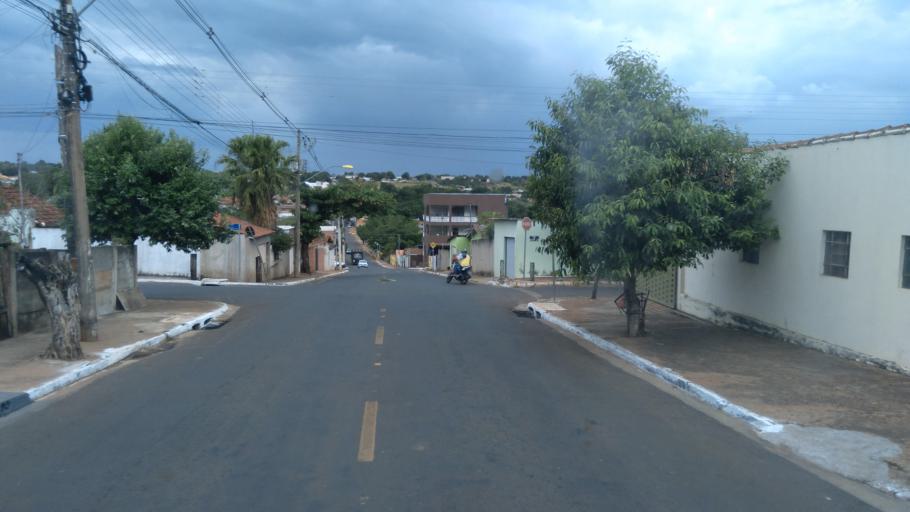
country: BR
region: Goias
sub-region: Mineiros
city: Mineiros
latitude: -17.5731
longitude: -52.5594
